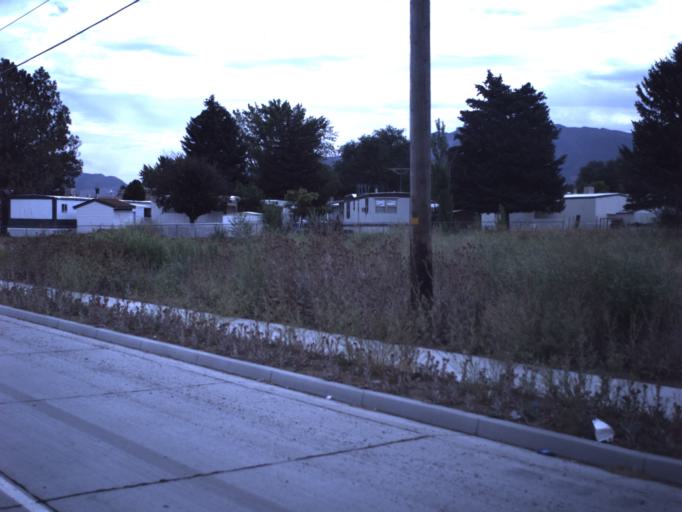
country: US
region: Utah
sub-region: Weber County
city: West Haven
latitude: 41.1928
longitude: -112.0459
